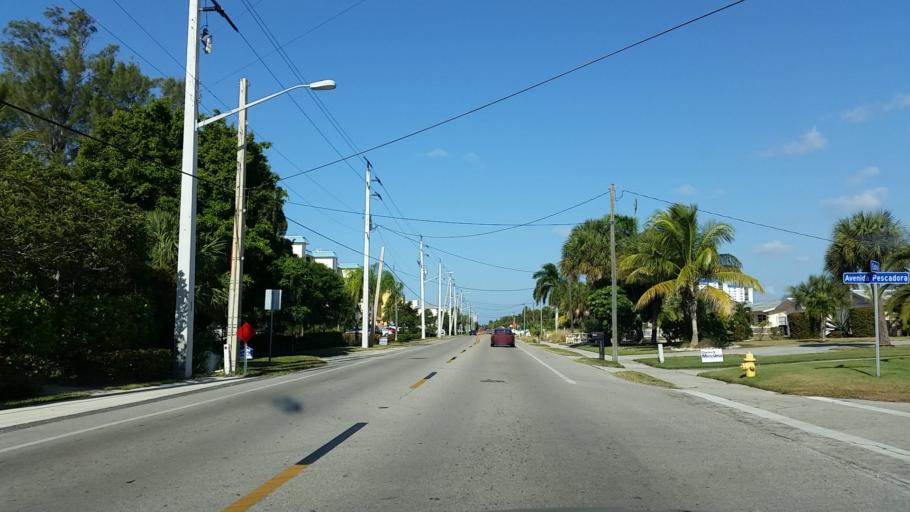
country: US
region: Florida
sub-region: Lee County
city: Fort Myers Beach
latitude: 26.4330
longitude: -81.9163
